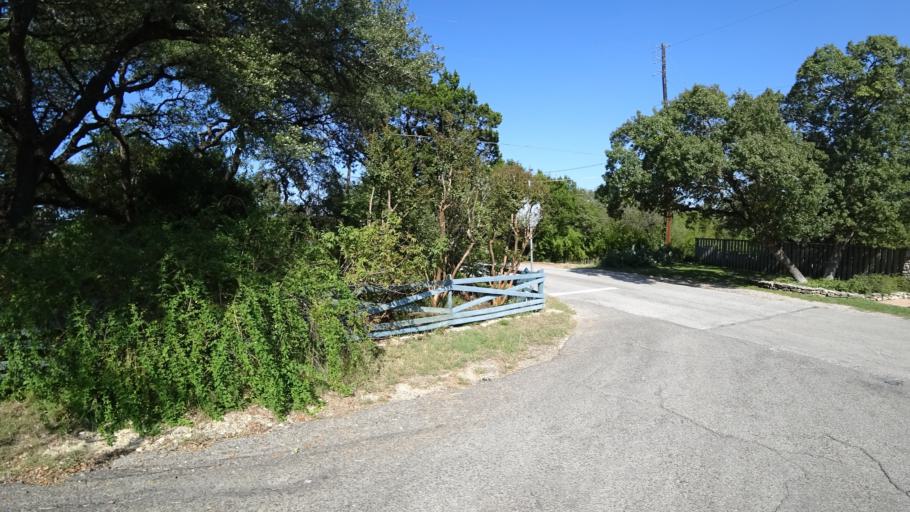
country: US
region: Texas
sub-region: Travis County
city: West Lake Hills
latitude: 30.2907
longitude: -97.8096
